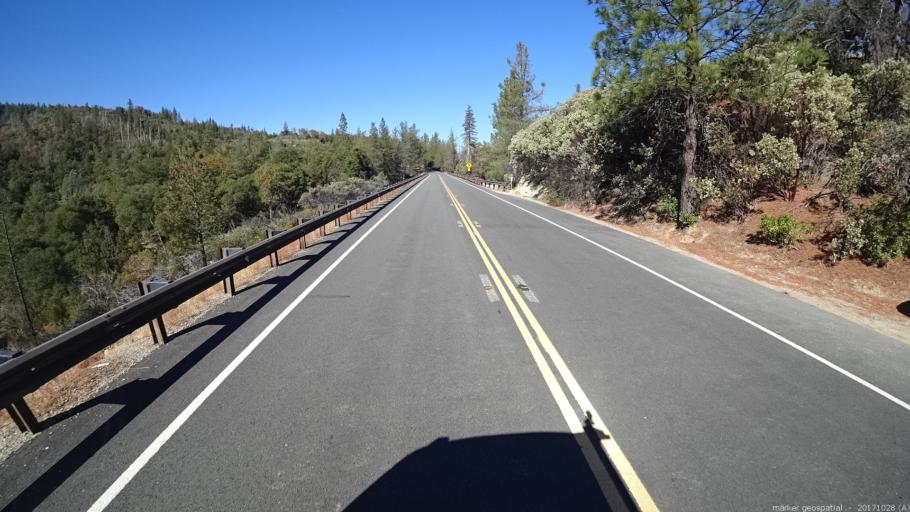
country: US
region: California
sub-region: Shasta County
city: Shasta
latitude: 40.5995
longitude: -122.5476
